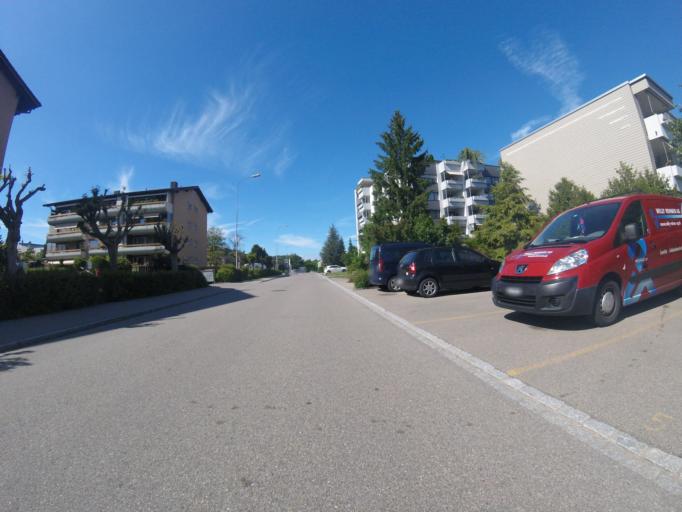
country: CH
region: Saint Gallen
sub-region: Wahlkreis Wil
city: Wil
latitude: 47.4524
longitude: 9.0476
